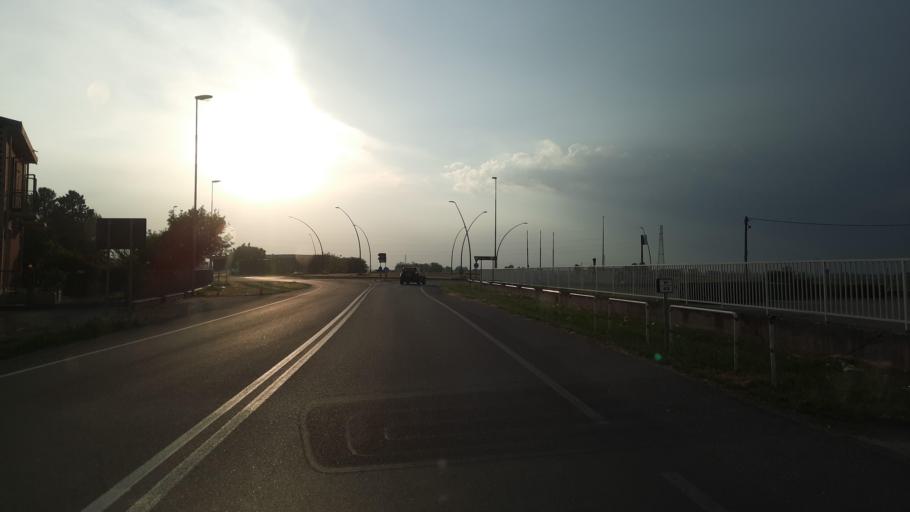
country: IT
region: Lombardy
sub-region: Provincia di Pavia
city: Mortara
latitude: 45.2490
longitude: 8.7208
